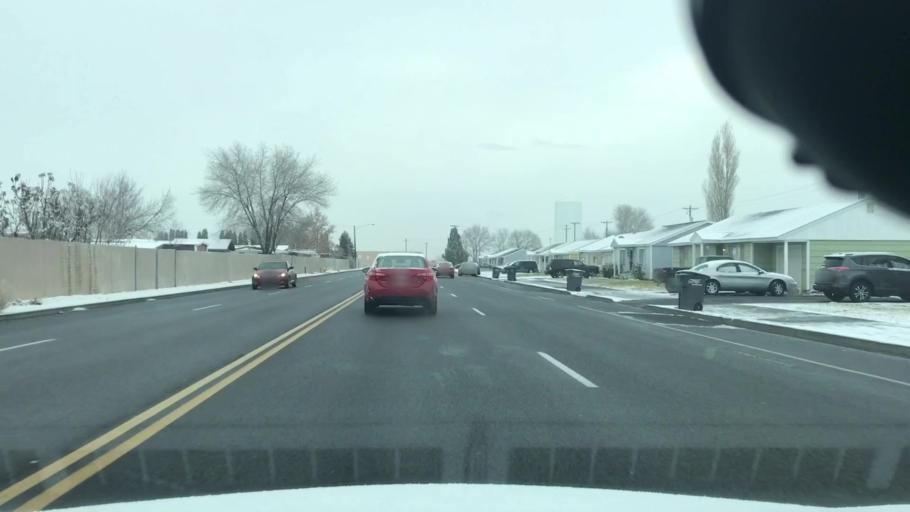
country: US
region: Washington
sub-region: Grant County
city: Moses Lake North
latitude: 47.1764
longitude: -119.3210
